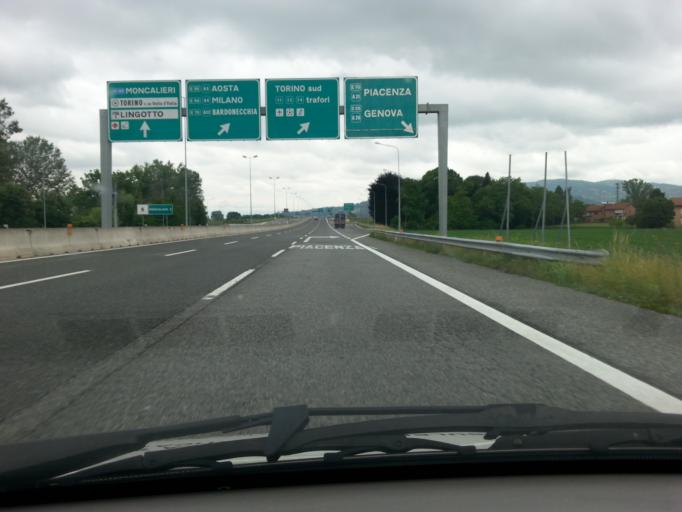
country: IT
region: Piedmont
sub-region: Provincia di Torino
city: La Loggia
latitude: 44.9657
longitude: 7.7040
